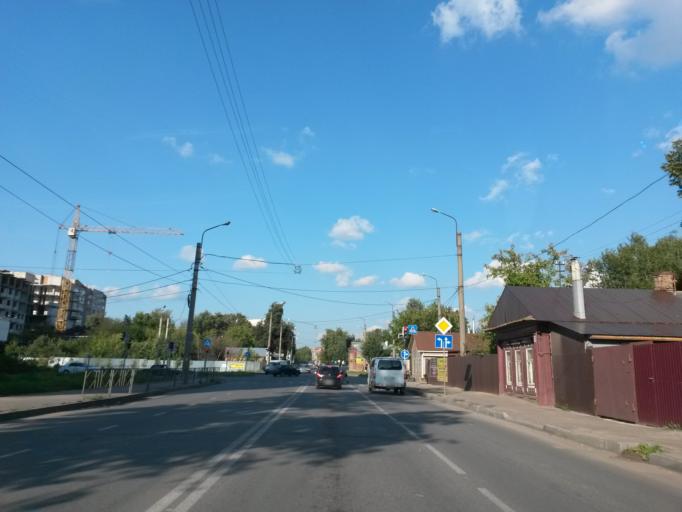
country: RU
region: Ivanovo
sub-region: Gorod Ivanovo
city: Ivanovo
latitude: 56.9925
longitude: 40.9663
